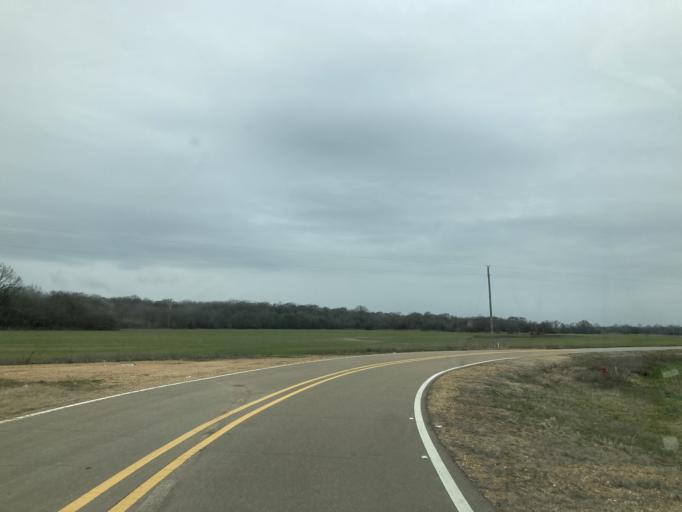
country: US
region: Mississippi
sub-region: Yazoo County
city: Yazoo City
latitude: 33.0094
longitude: -90.4700
